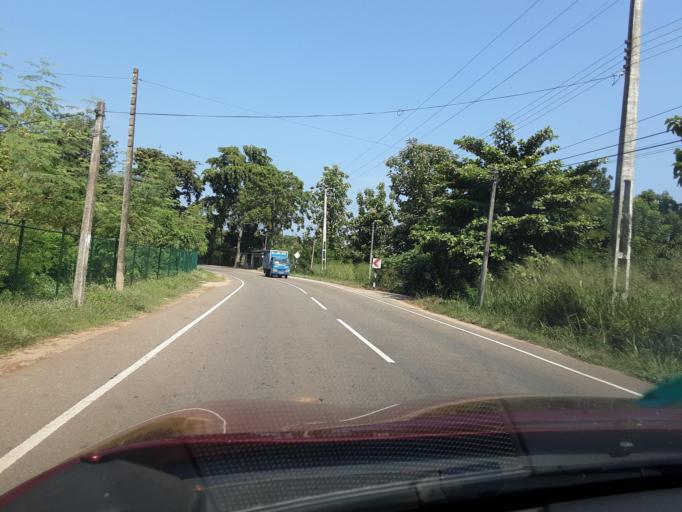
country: LK
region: Uva
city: Badulla
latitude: 7.1954
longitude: 81.0210
